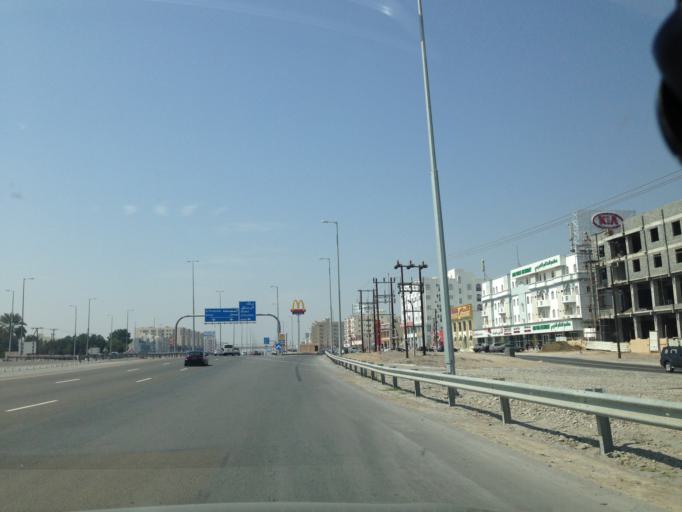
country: OM
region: Al Batinah
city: Barka'
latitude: 23.6642
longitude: 57.8998
